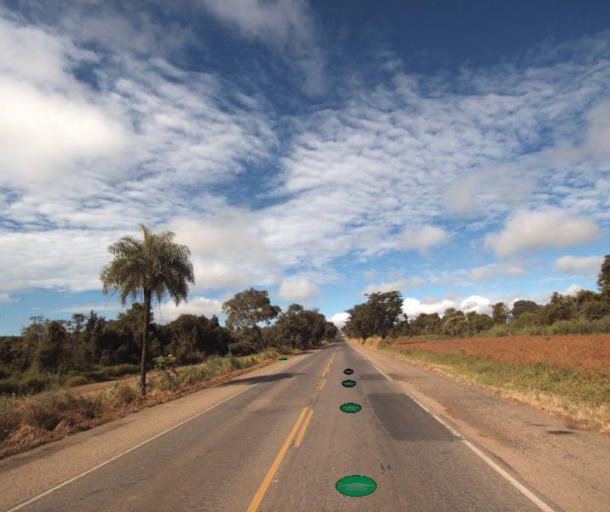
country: BR
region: Goias
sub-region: Uruacu
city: Uruacu
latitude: -14.6729
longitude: -49.2009
